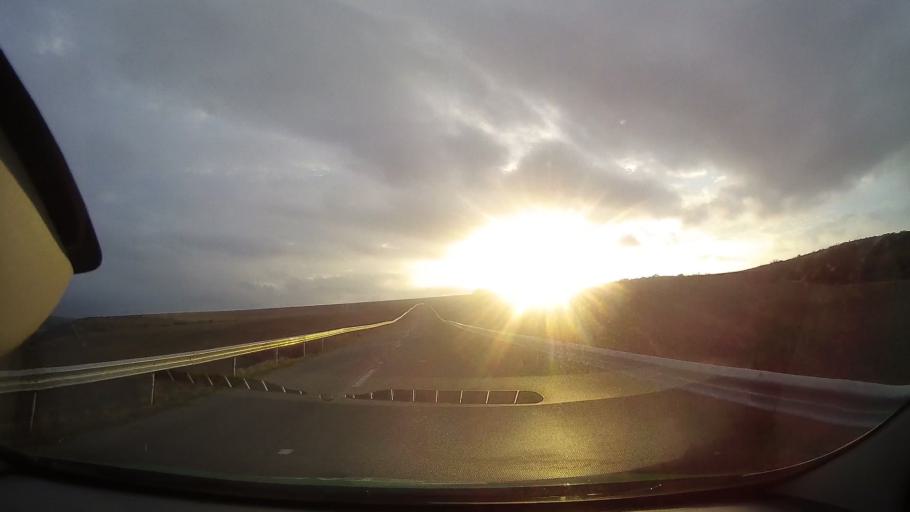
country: RO
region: Constanta
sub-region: Comuna Adamclisi
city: Adamclisi
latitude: 44.0378
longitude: 27.9406
